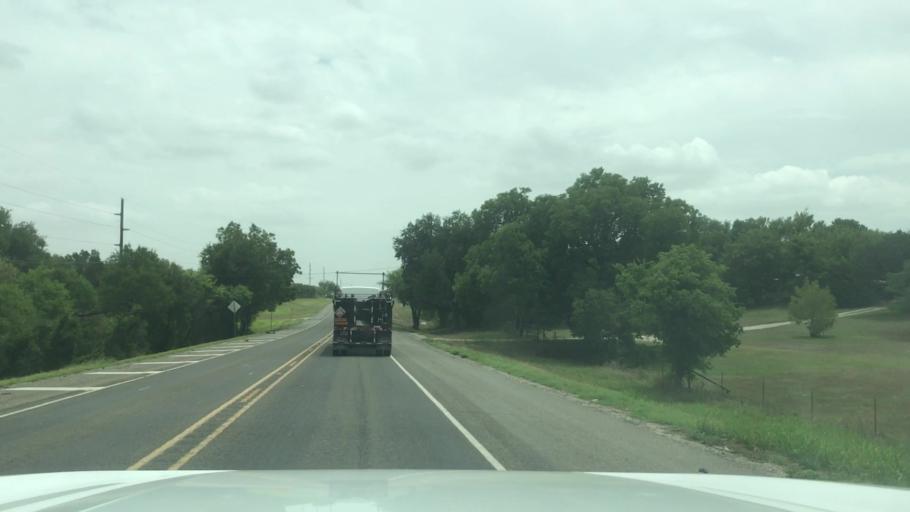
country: US
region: Texas
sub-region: Bosque County
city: Valley Mills
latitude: 31.6929
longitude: -97.5348
